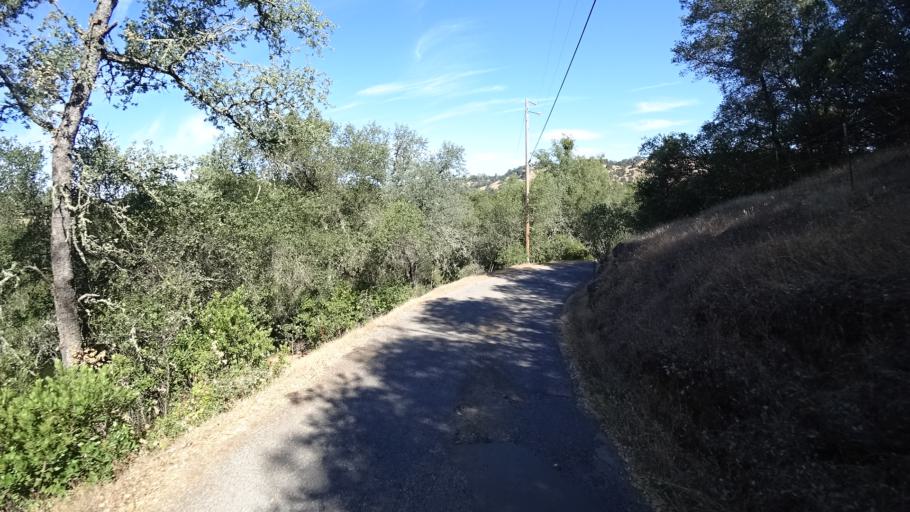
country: US
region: California
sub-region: Calaveras County
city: San Andreas
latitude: 38.1535
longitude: -120.6148
